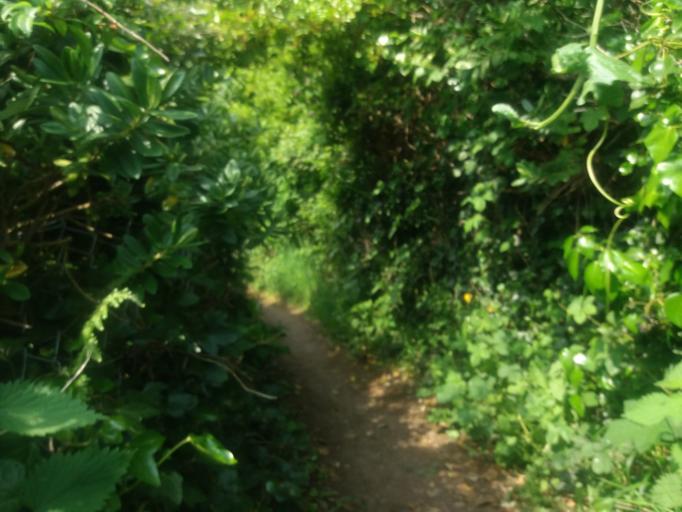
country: IE
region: Leinster
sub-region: Fingal County
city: Howth
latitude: 53.3641
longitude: -6.0626
